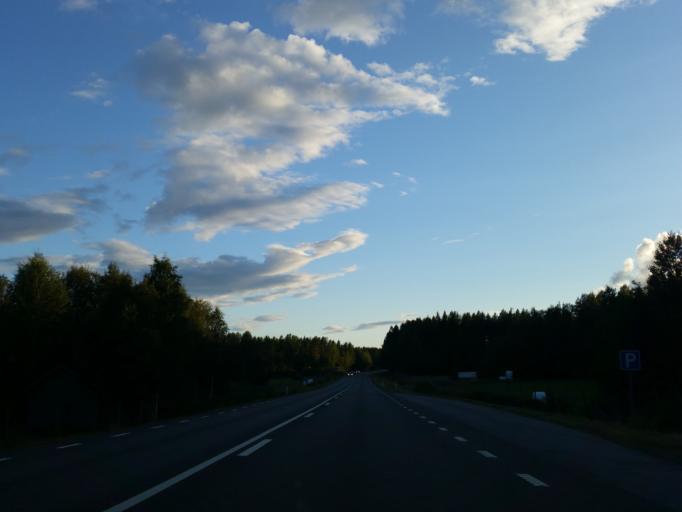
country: SE
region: Vaesterbotten
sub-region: Robertsfors Kommun
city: Robertsfors
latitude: 64.0041
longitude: 20.7993
